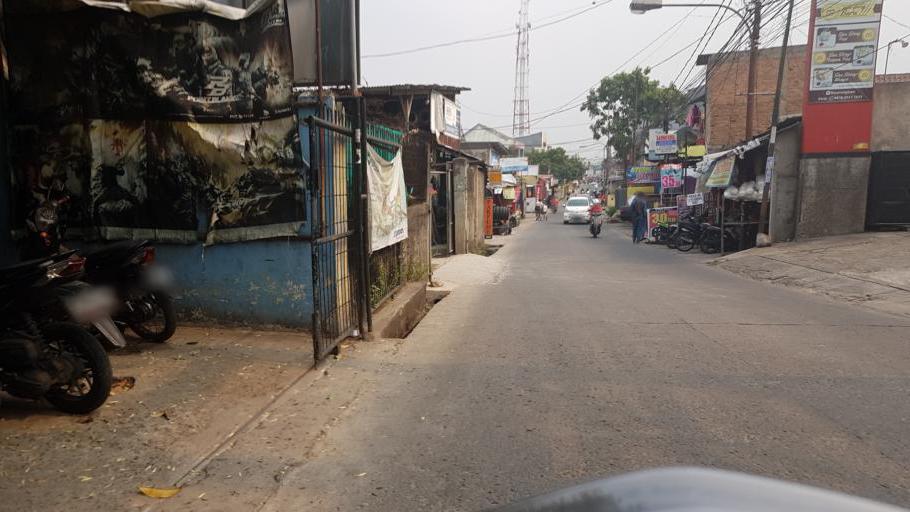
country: ID
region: West Java
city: Depok
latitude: -6.3585
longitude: 106.8431
